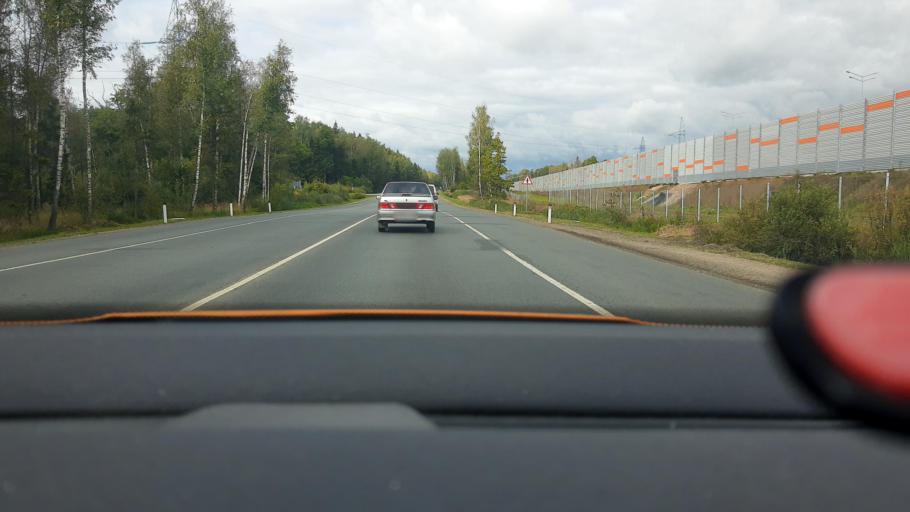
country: RU
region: Moskovskaya
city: Zelenogradskiy
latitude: 56.0875
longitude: 37.9945
